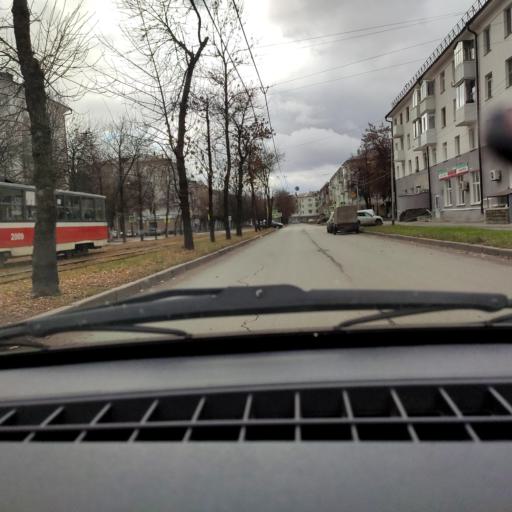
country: RU
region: Bashkortostan
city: Ufa
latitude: 54.8214
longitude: 56.0653
